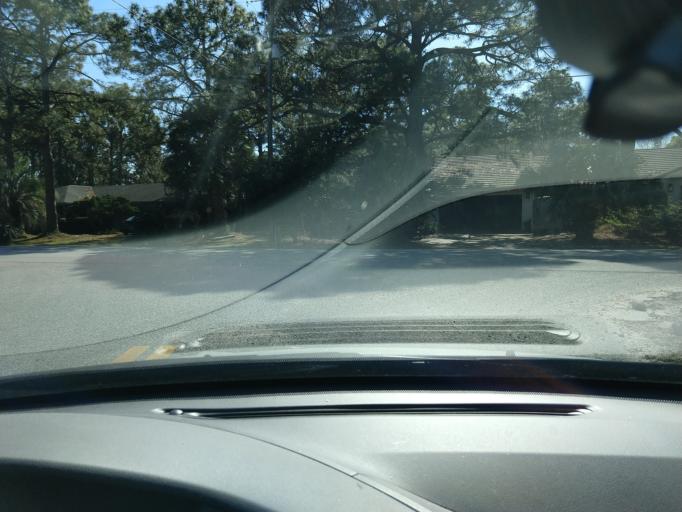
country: US
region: Florida
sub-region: Walton County
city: Miramar Beach
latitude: 30.3874
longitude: -86.3726
